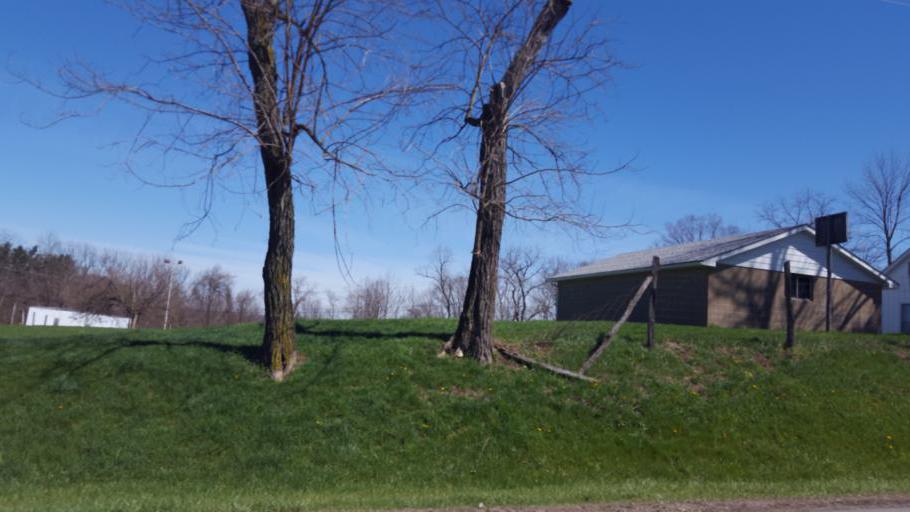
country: US
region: Ohio
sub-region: Belmont County
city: Saint Clairsville
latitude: 40.0778
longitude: -80.9124
